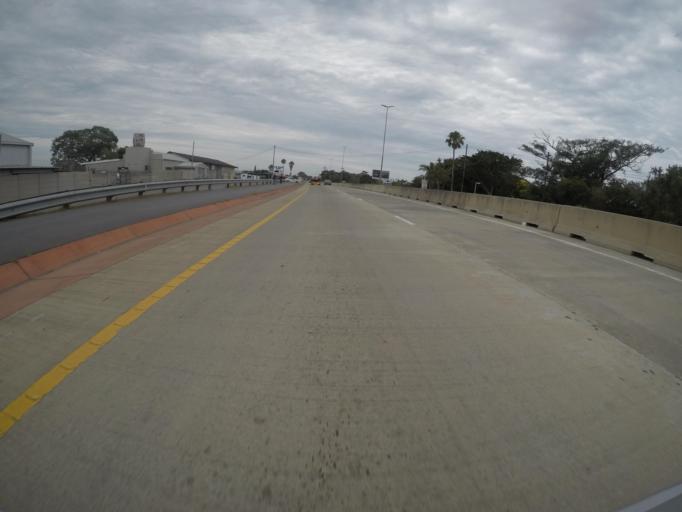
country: ZA
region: Eastern Cape
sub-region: Buffalo City Metropolitan Municipality
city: East London
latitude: -32.9423
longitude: 27.9708
